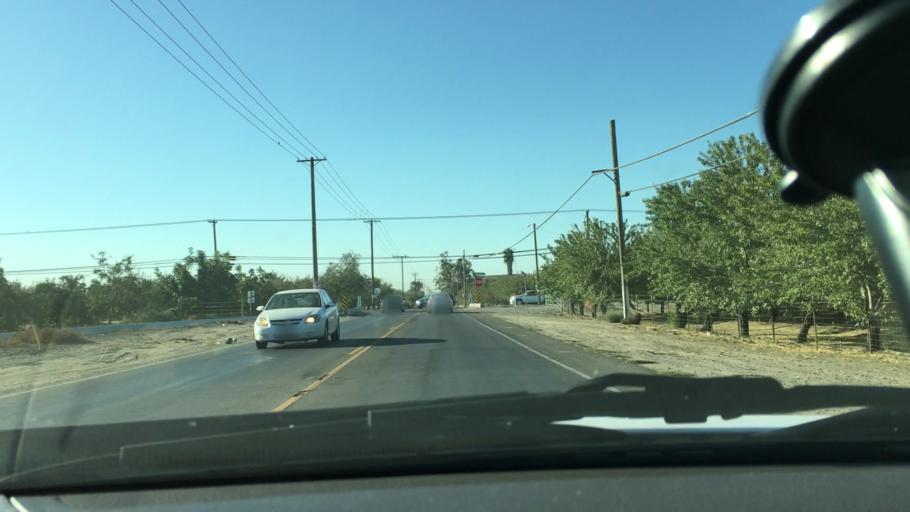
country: US
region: California
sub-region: Stanislaus County
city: West Modesto
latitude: 37.5960
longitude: -121.0303
